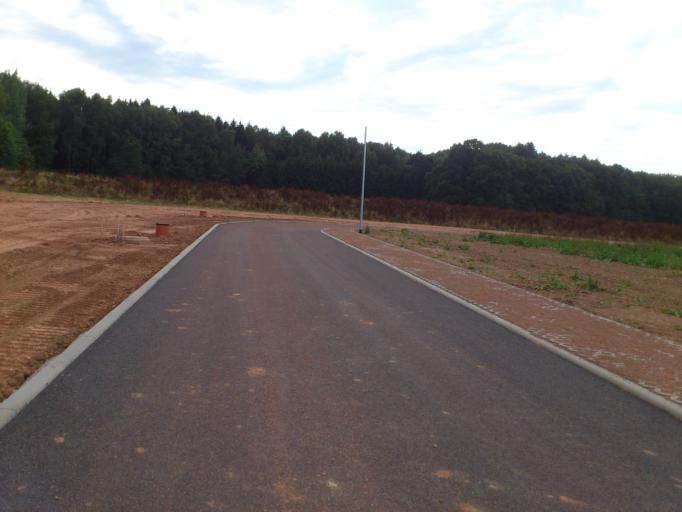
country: DE
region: Saxony
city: Neukirchen
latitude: 50.7770
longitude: 12.8453
